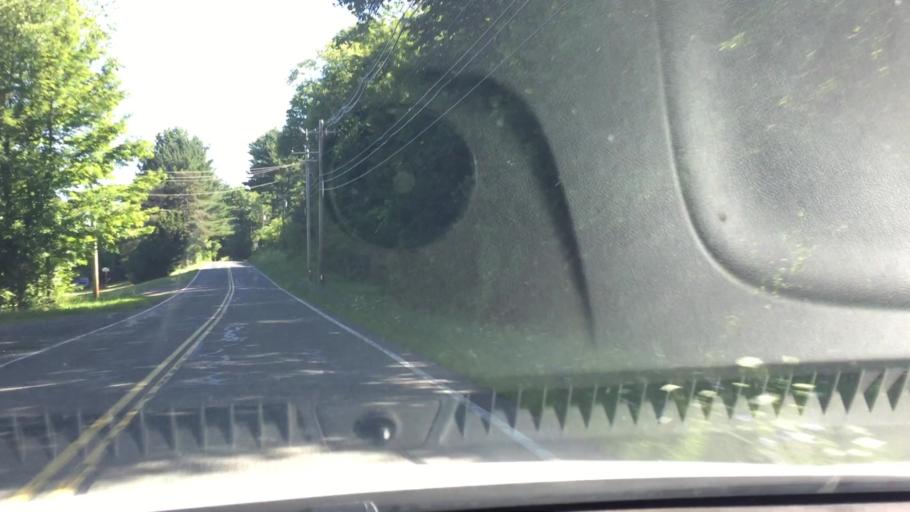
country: US
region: Massachusetts
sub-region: Berkshire County
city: West Stockbridge
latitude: 42.3423
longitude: -73.3658
